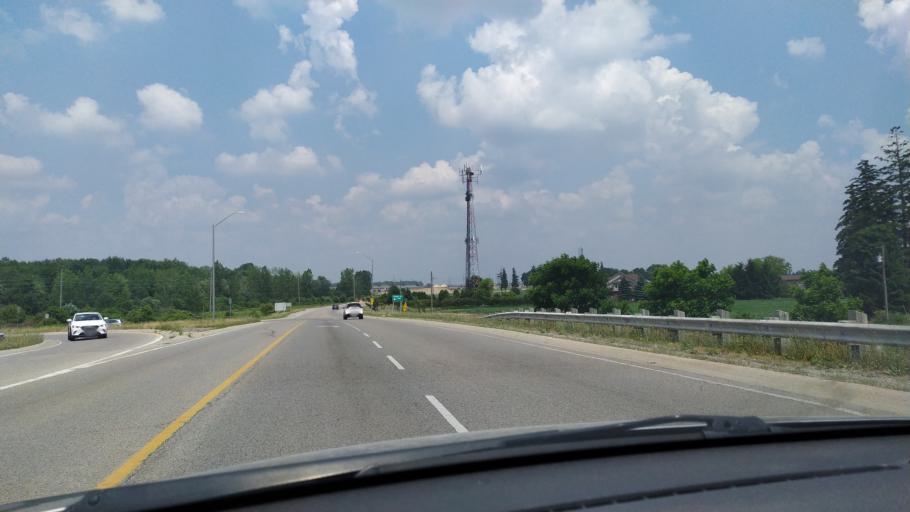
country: CA
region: Ontario
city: London
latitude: 42.9455
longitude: -81.1838
